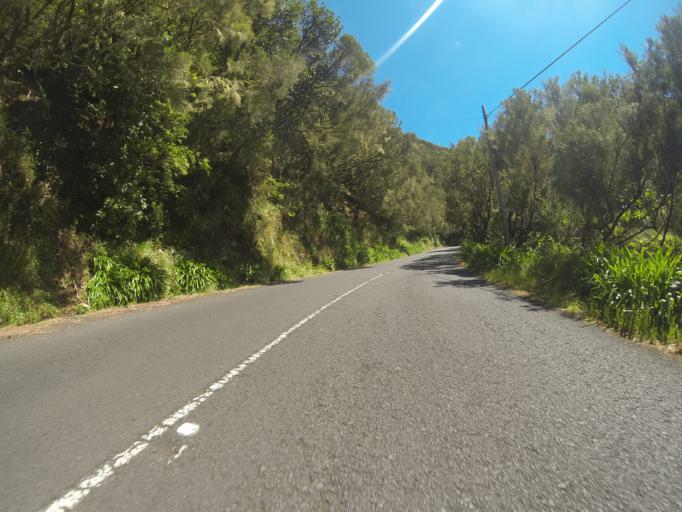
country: PT
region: Madeira
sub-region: Funchal
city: Nossa Senhora do Monte
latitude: 32.7259
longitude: -16.8889
